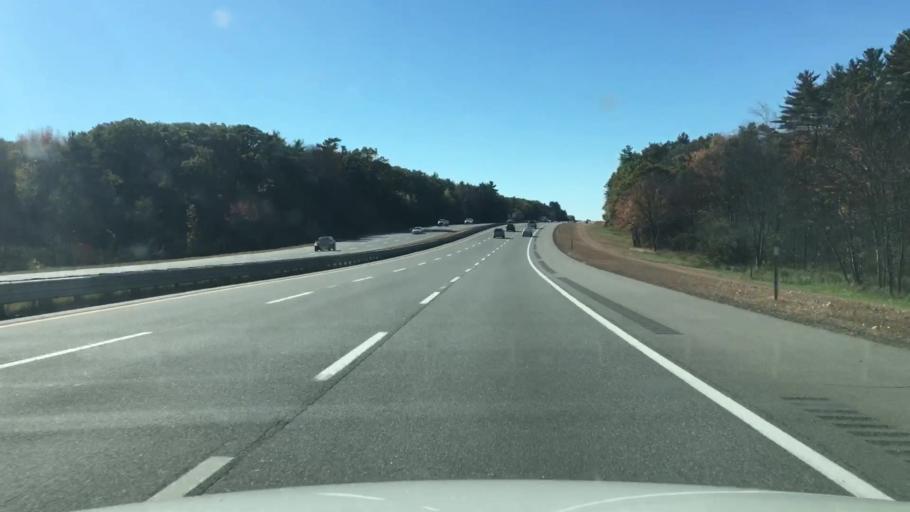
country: US
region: Maine
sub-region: York County
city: Cape Neddick
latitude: 43.1889
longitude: -70.6459
